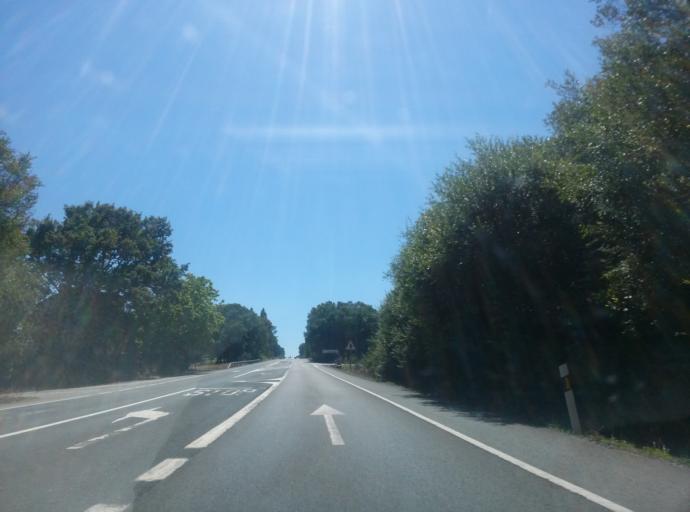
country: ES
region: Galicia
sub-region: Provincia de Lugo
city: Mos
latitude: 43.1114
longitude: -7.4536
